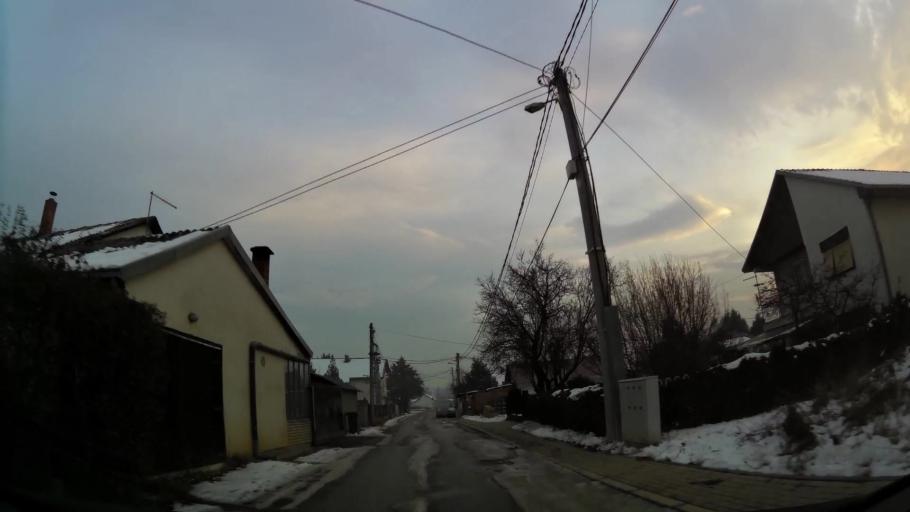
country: MK
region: Suto Orizari
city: Suto Orizare
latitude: 42.0381
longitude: 21.4076
